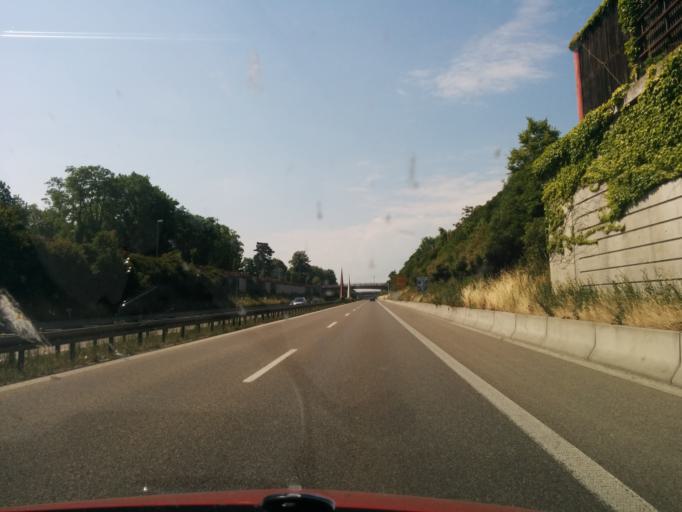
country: DE
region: Bavaria
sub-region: Swabia
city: Klosterlechfeld
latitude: 48.1831
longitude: 10.8447
